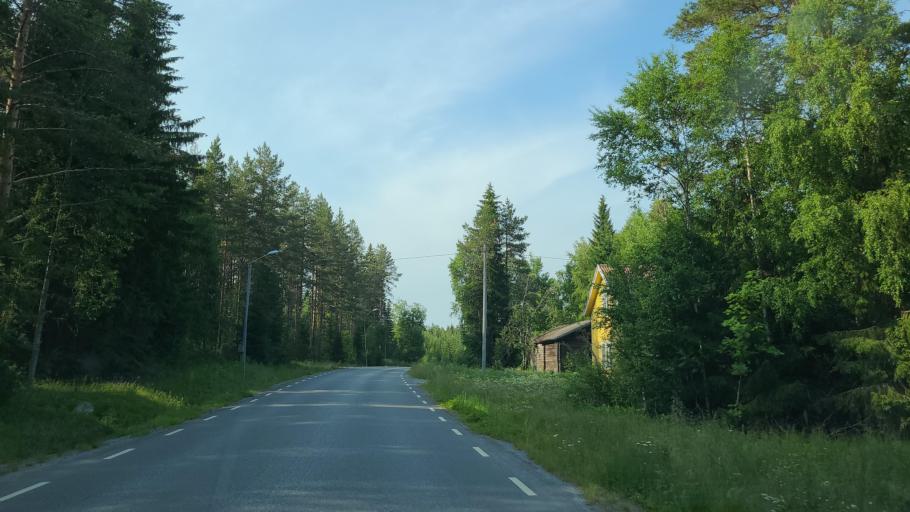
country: SE
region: Vaesterbotten
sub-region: Skelleftea Kommun
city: Burea
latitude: 64.4489
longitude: 21.3538
